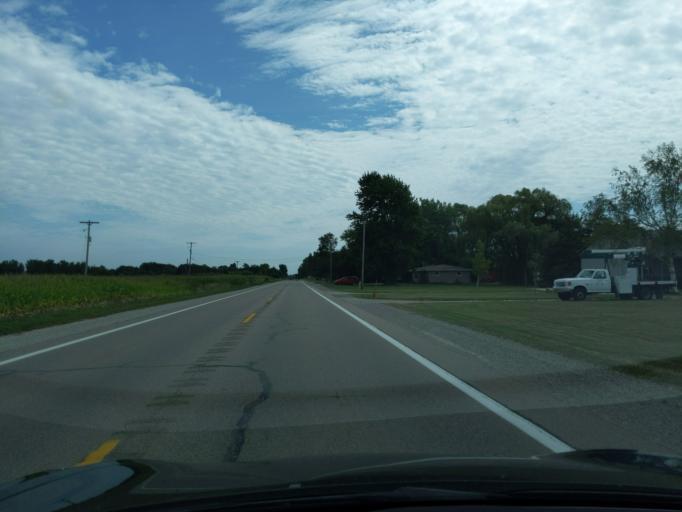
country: US
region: Michigan
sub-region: Gratiot County
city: Breckenridge
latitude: 43.4080
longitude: -84.3982
